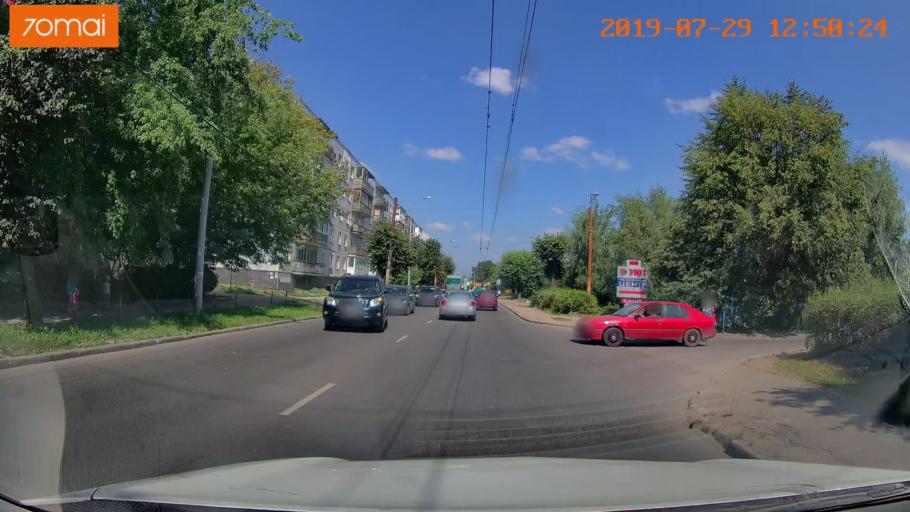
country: RU
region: Kaliningrad
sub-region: Gorod Kaliningrad
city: Kaliningrad
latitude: 54.6869
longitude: 20.5329
